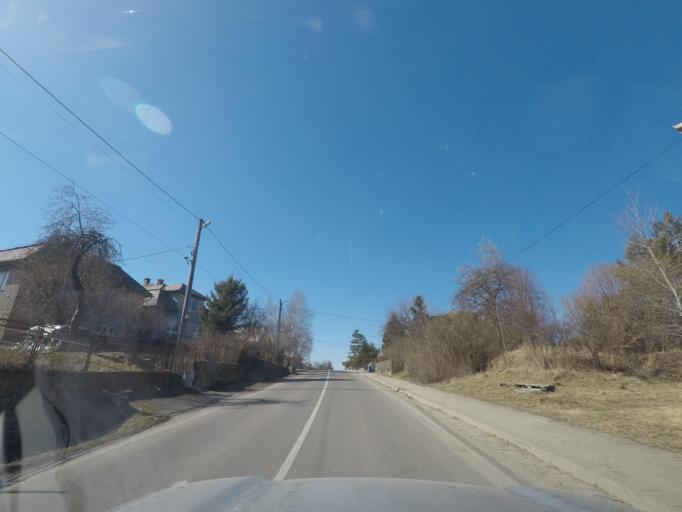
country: UA
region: Zakarpattia
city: Velykyi Bereznyi
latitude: 48.8934
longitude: 22.4084
